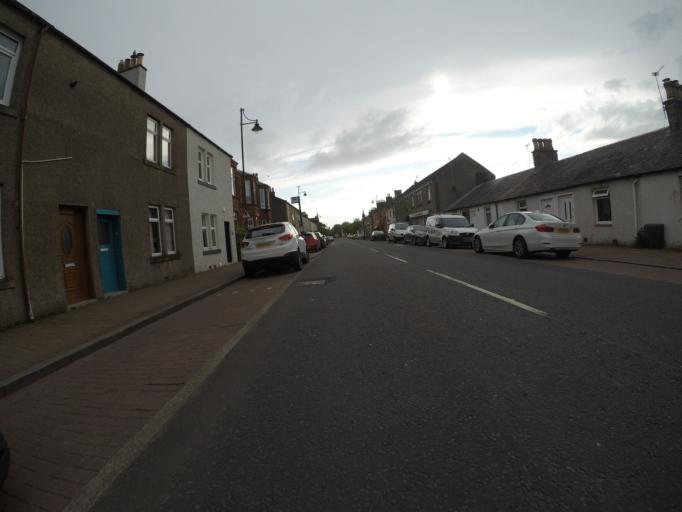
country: GB
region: Scotland
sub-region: North Ayrshire
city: Dreghorn
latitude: 55.6105
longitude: -4.6147
